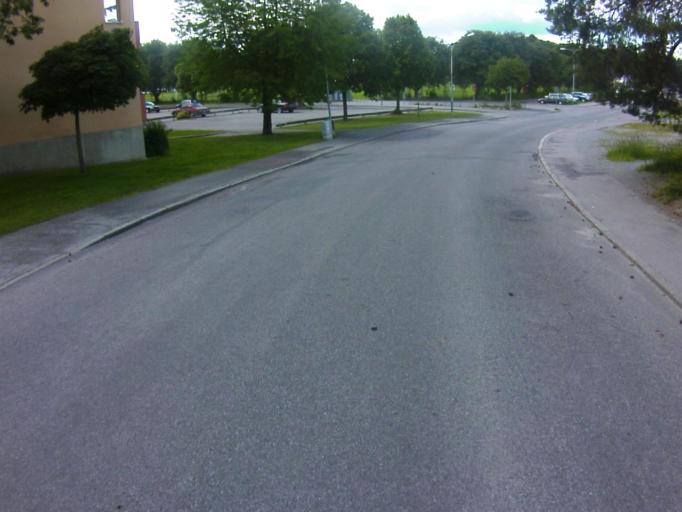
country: SE
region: Soedermanland
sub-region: Eskilstuna Kommun
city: Eskilstuna
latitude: 59.3550
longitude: 16.4915
